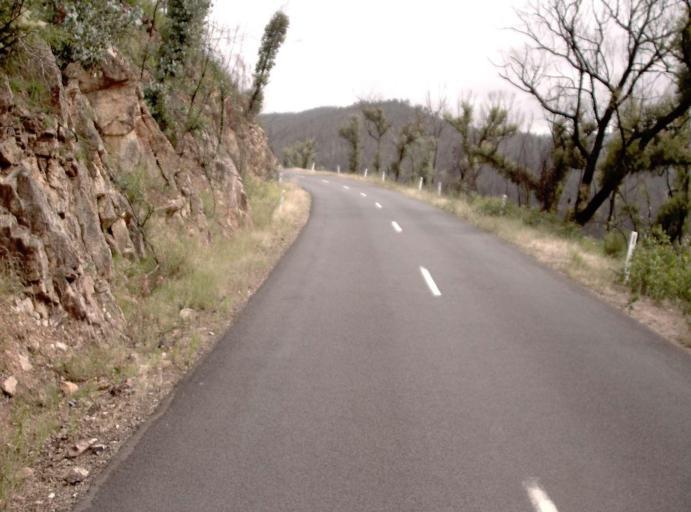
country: AU
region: Victoria
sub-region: Wellington
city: Heyfield
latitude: -37.7301
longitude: 146.6702
